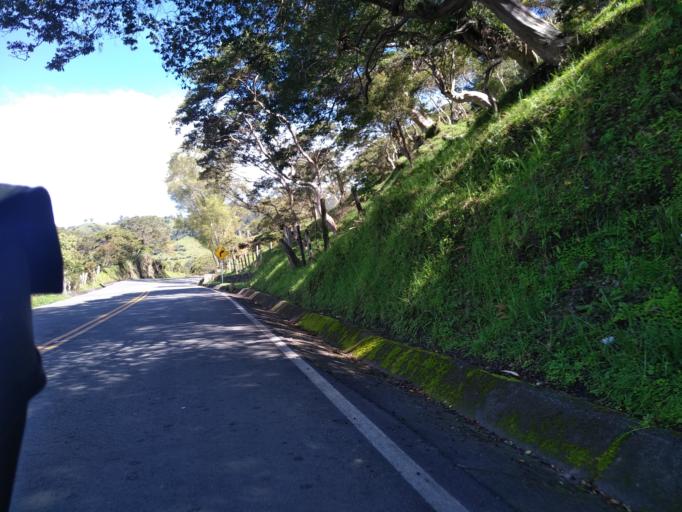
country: CO
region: Santander
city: Velez
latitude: 5.9989
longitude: -73.6891
